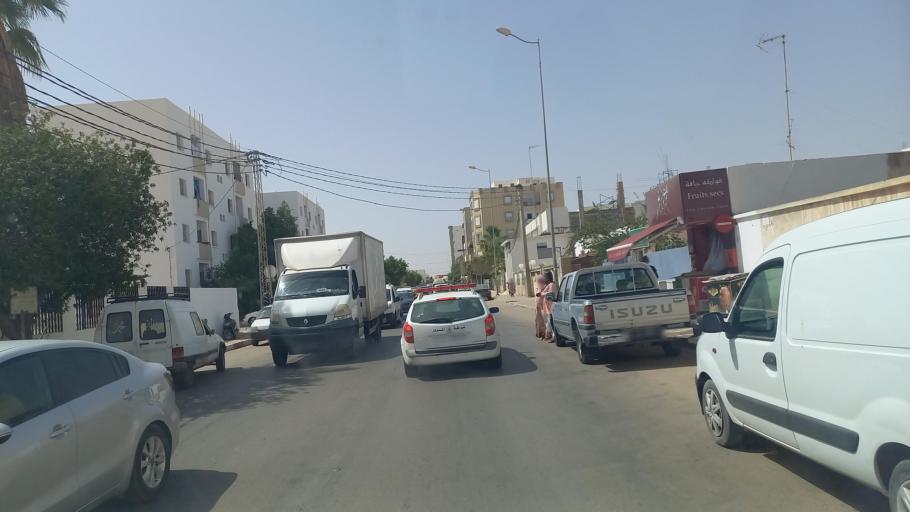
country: TN
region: Madanin
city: Medenine
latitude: 33.3414
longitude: 10.4882
